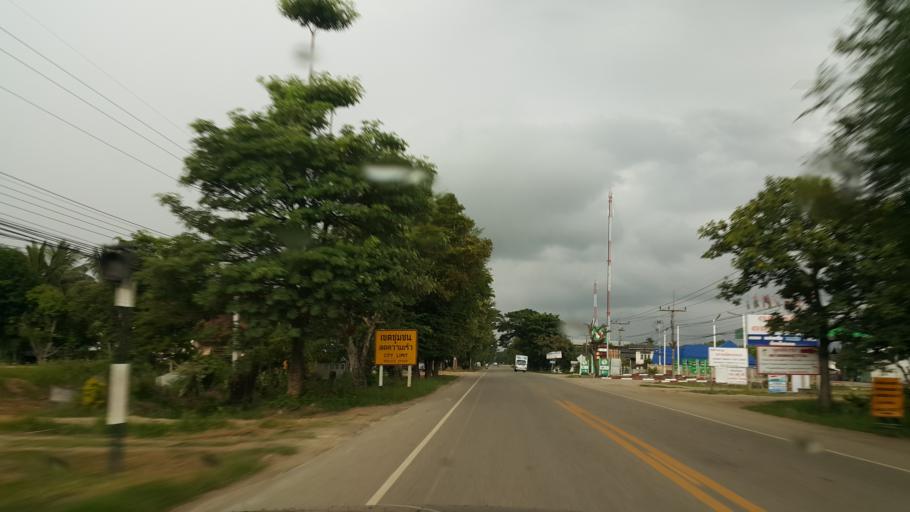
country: TH
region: Phayao
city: Phu Kam Yao
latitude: 19.2329
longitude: 100.0490
